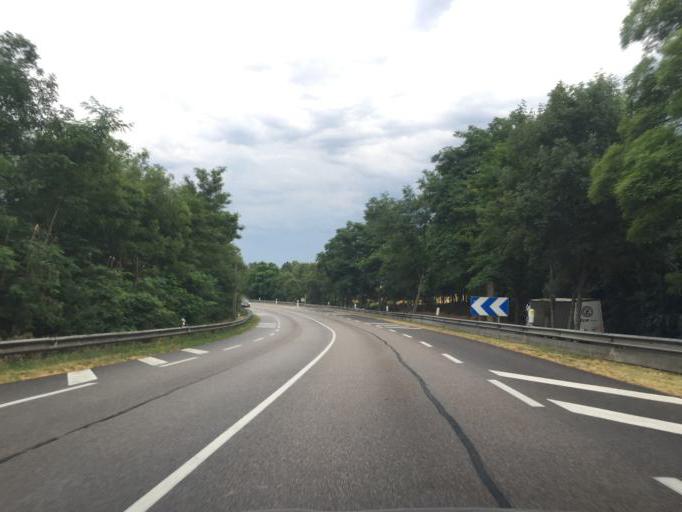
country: FR
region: Rhone-Alpes
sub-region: Departement de la Loire
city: La Pacaudiere
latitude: 46.1985
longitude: 3.8326
